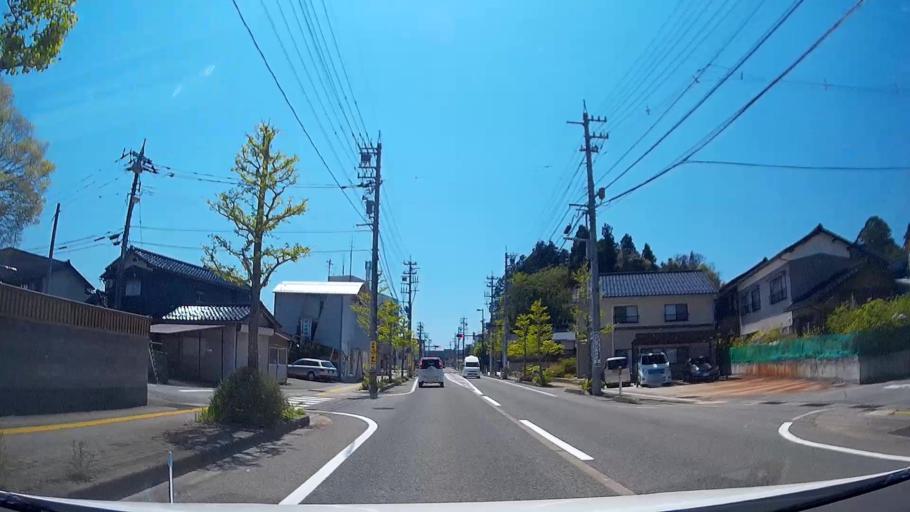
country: JP
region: Ishikawa
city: Nanao
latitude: 37.4375
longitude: 137.2616
